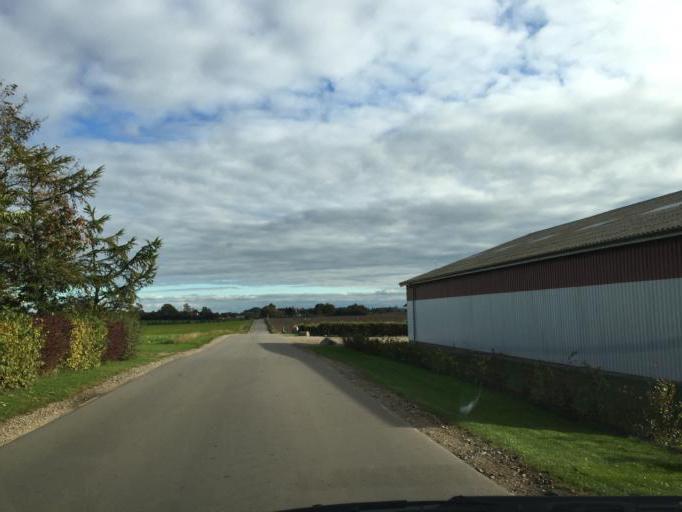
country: DK
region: Zealand
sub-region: Odsherred Kommune
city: Horve
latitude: 55.7537
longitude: 11.3688
